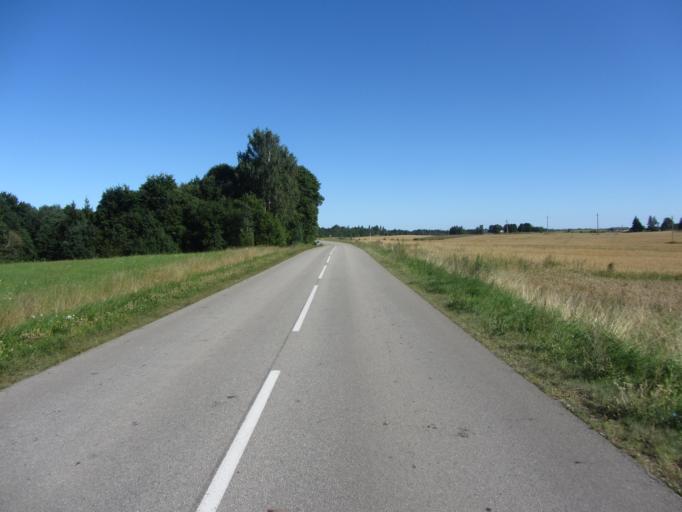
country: LT
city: Kupiskis
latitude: 55.8277
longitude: 25.0605
